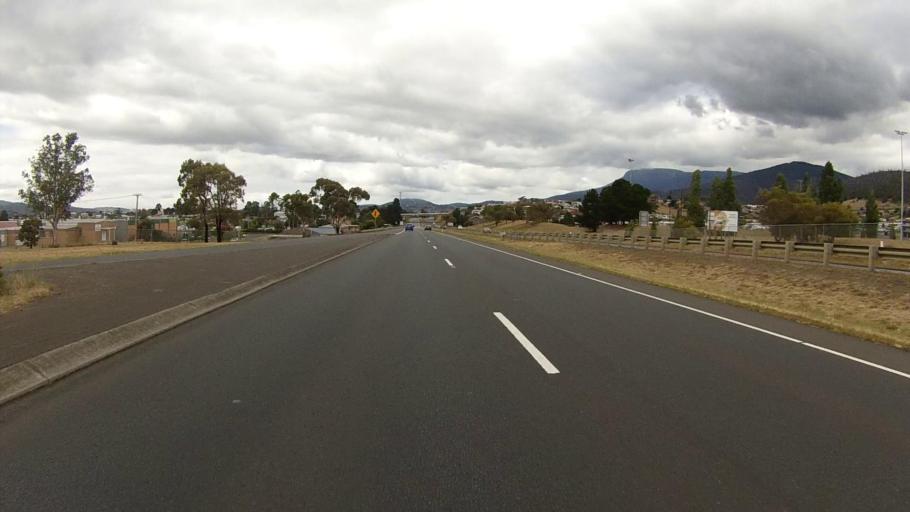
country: AU
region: Tasmania
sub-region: Glenorchy
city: Claremont
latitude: -42.7887
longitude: 147.2448
